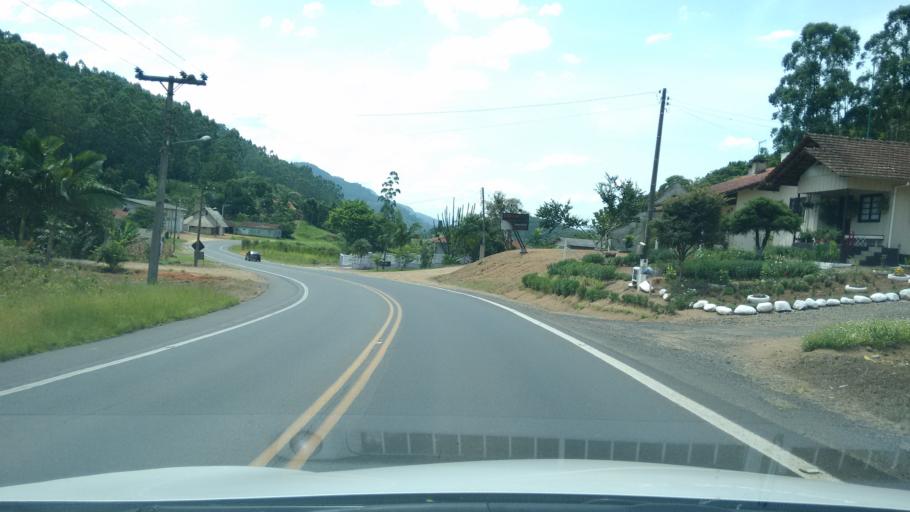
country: BR
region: Santa Catarina
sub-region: Rodeio
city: Gavea
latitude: -26.8942
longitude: -49.3514
